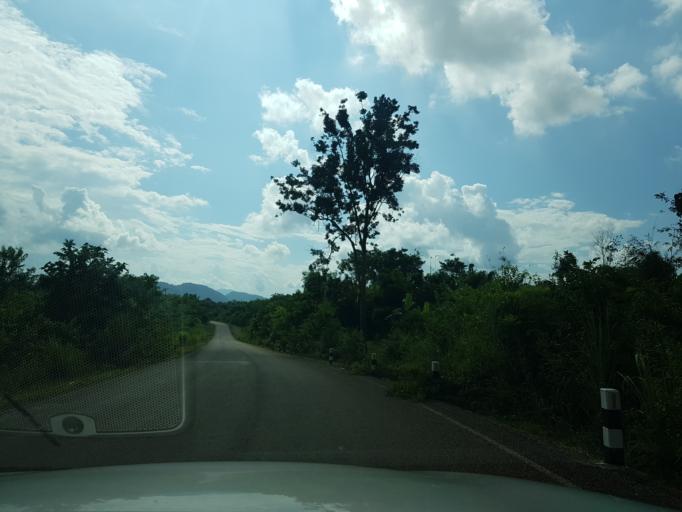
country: TH
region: Nong Khai
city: Sangkhom
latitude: 18.1900
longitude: 102.1990
